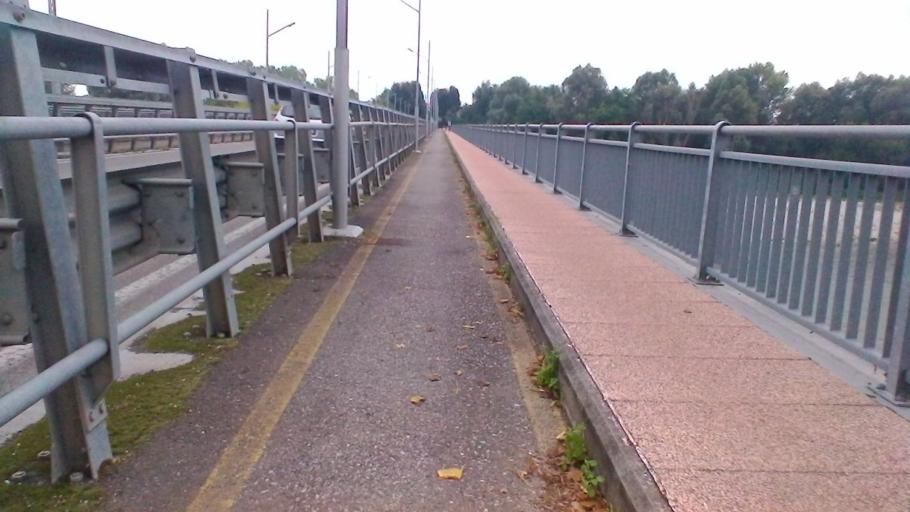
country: IT
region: Veneto
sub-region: Provincia di Verona
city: Zevio
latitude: 45.3813
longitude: 11.1352
